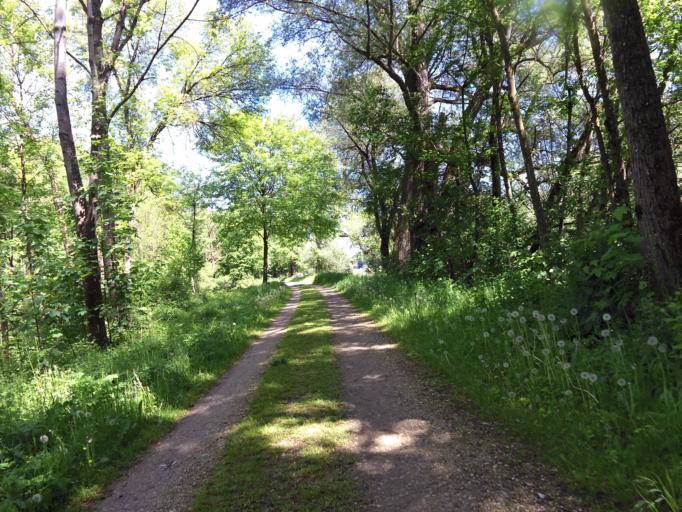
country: DE
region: Bavaria
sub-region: Upper Bavaria
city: Marzling
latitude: 48.4064
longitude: 11.8183
